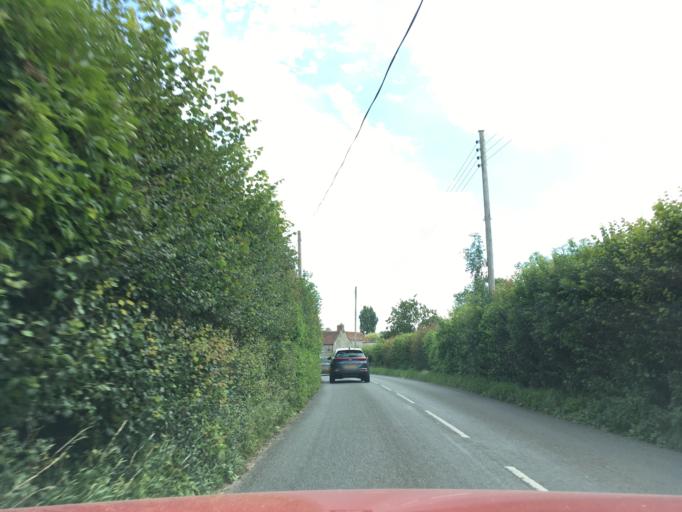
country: GB
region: England
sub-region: Somerset
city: Street
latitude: 51.0991
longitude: -2.6872
